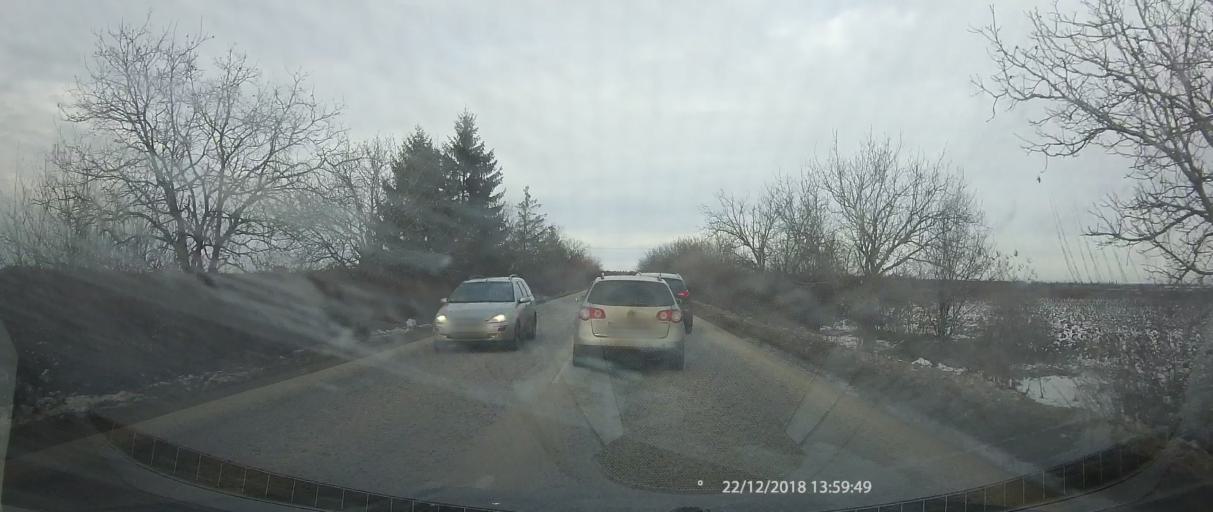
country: BG
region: Pleven
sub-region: Obshtina Dolni Dubnik
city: Dolni Dubnik
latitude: 43.3532
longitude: 24.3436
